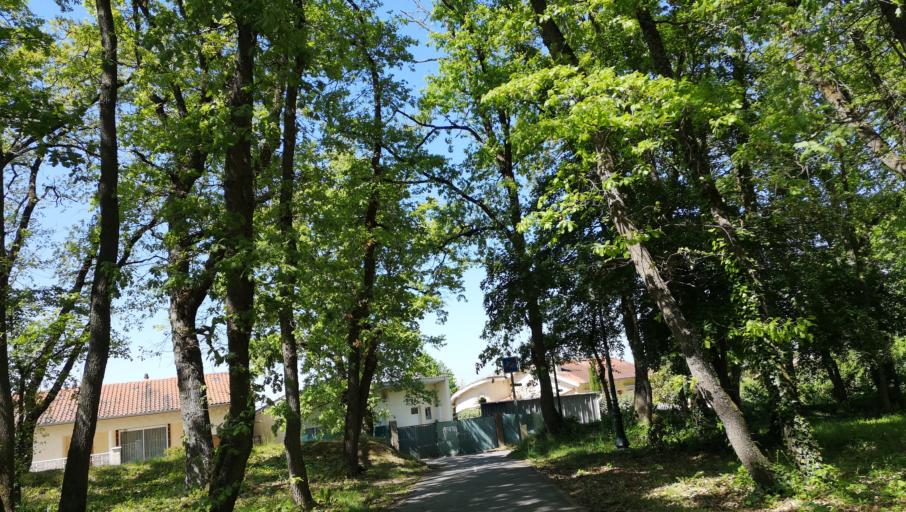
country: FR
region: Midi-Pyrenees
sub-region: Departement de la Haute-Garonne
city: Seilh
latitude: 43.6891
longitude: 1.3611
